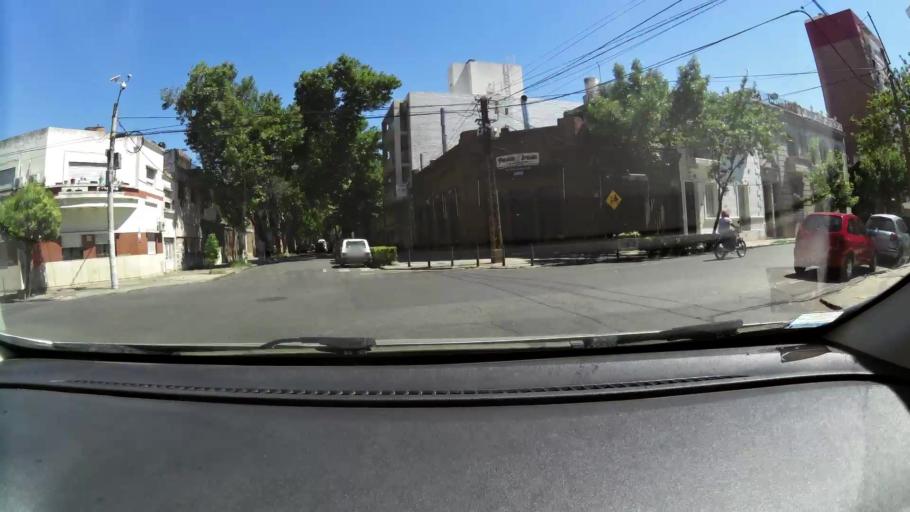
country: AR
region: Santa Fe
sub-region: Departamento de Rosario
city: Rosario
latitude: -32.9374
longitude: -60.6546
